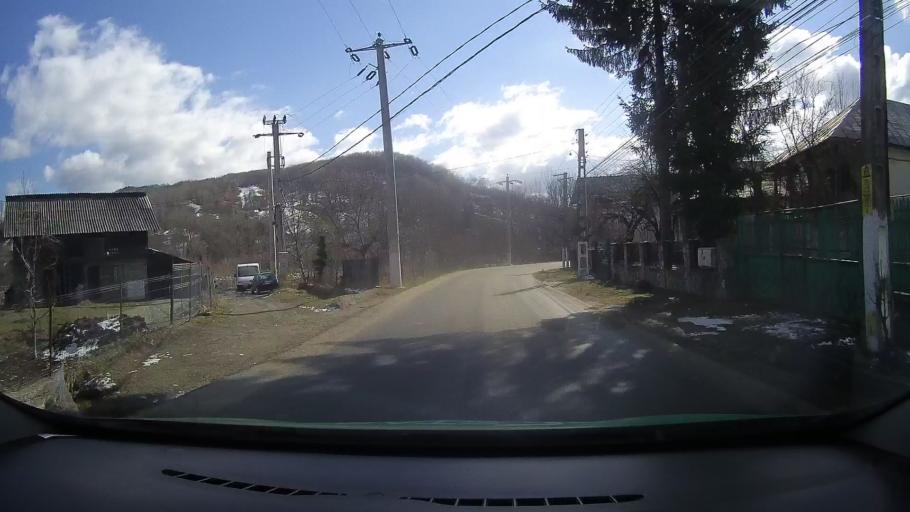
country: RO
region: Dambovita
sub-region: Comuna Runcu
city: Runcu
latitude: 45.1710
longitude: 25.3937
